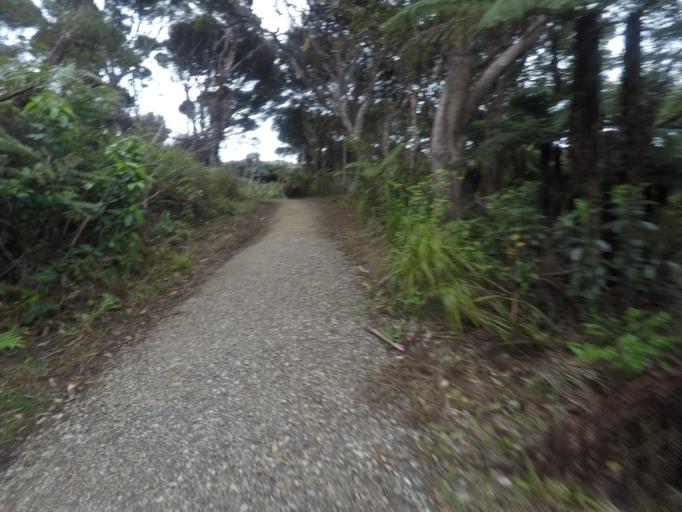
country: NZ
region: Auckland
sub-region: Auckland
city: Muriwai Beach
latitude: -36.9756
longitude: 174.4734
